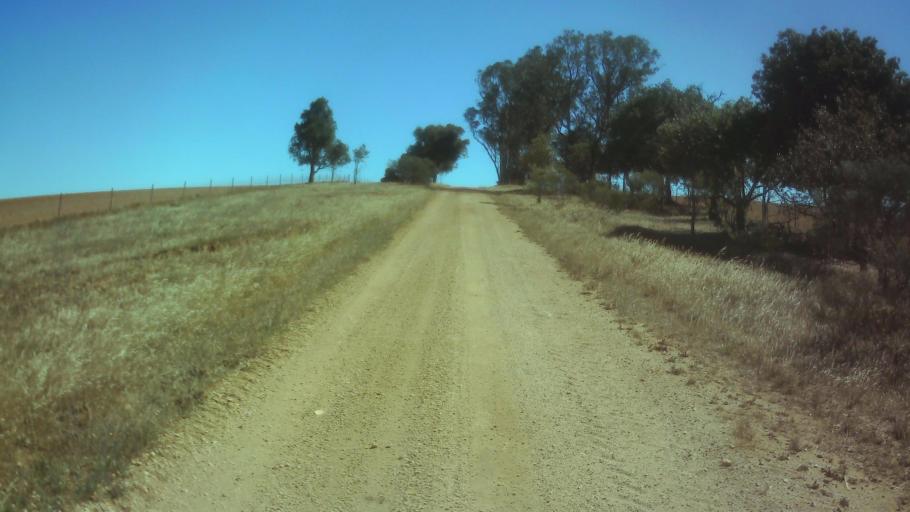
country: AU
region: New South Wales
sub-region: Weddin
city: Grenfell
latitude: -33.9777
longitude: 148.3424
